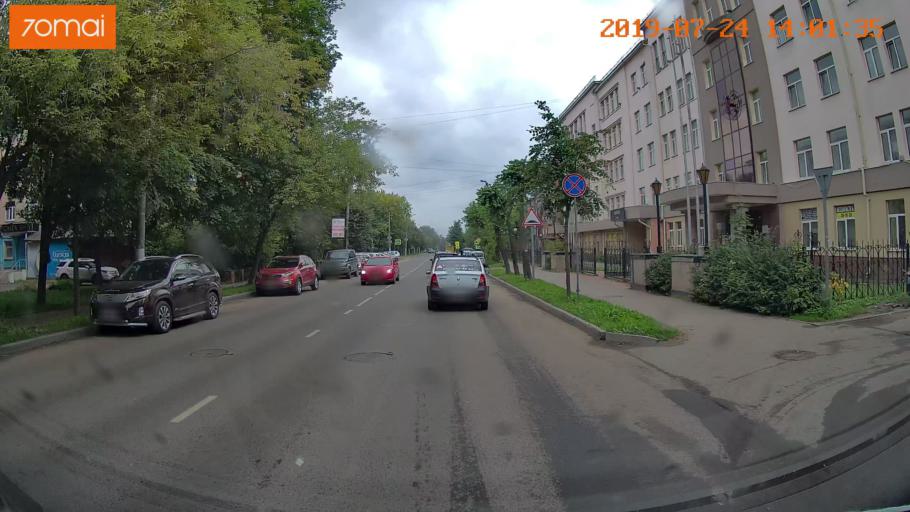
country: RU
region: Ivanovo
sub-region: Gorod Ivanovo
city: Ivanovo
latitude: 57.0092
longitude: 40.9796
